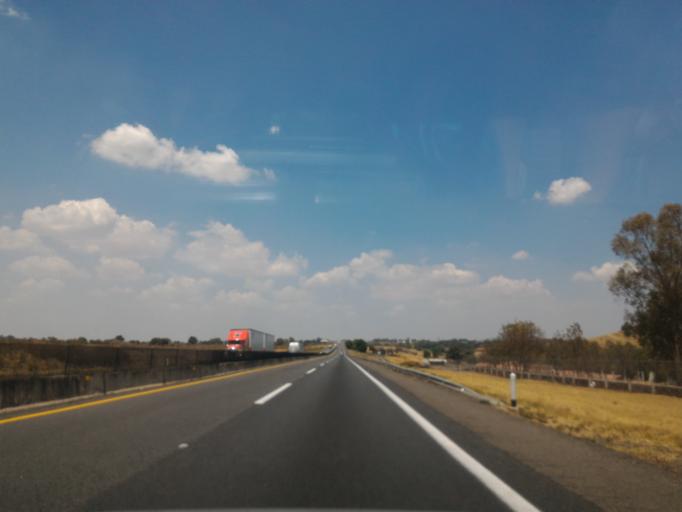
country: MX
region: Jalisco
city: Tepatitlan de Morelos
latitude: 20.8756
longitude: -102.7417
